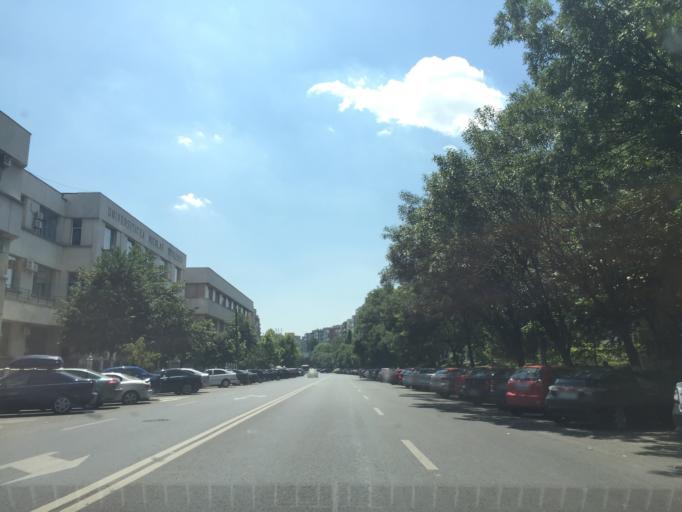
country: RO
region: Bucuresti
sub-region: Municipiul Bucuresti
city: Bucharest
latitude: 44.4148
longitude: 26.1137
